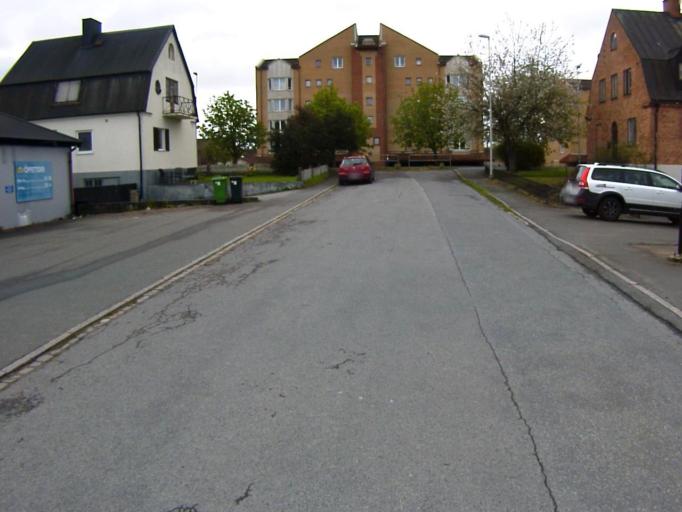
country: SE
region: Skane
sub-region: Kristianstads Kommun
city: Kristianstad
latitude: 56.0214
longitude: 14.1398
